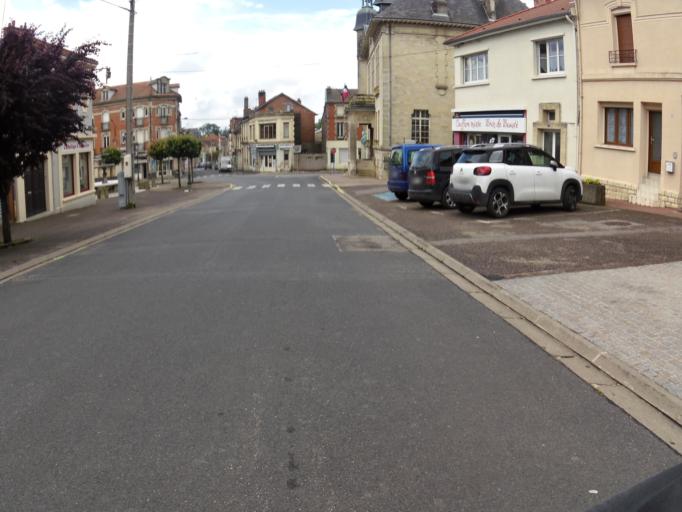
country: FR
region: Champagne-Ardenne
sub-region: Departement de la Marne
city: Sermaize-les-Bains
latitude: 48.7840
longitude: 4.9124
